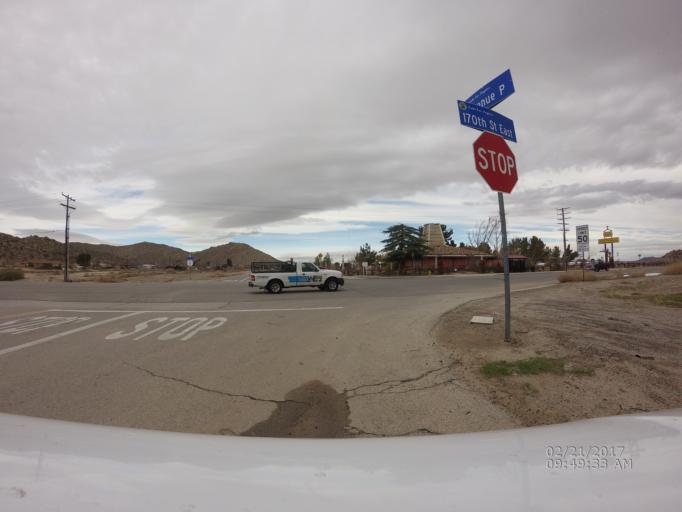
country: US
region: California
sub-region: Los Angeles County
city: Lake Los Angeles
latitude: 34.6006
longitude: -117.8252
